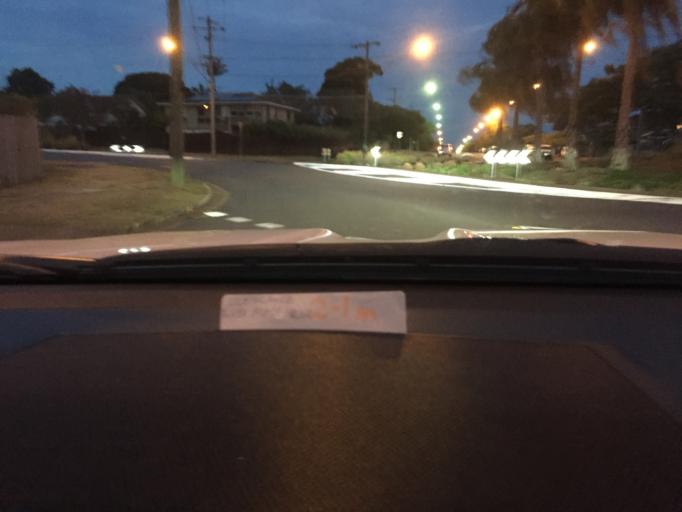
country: AU
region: Queensland
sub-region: Moreton Bay
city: Margate
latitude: -27.2419
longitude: 153.0860
